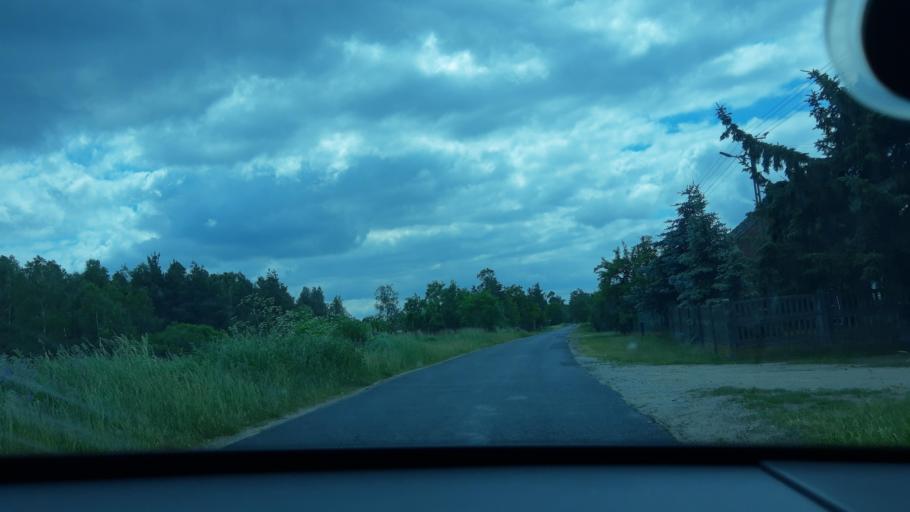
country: PL
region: Lodz Voivodeship
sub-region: Powiat sieradzki
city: Burzenin
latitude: 51.5057
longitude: 18.8472
